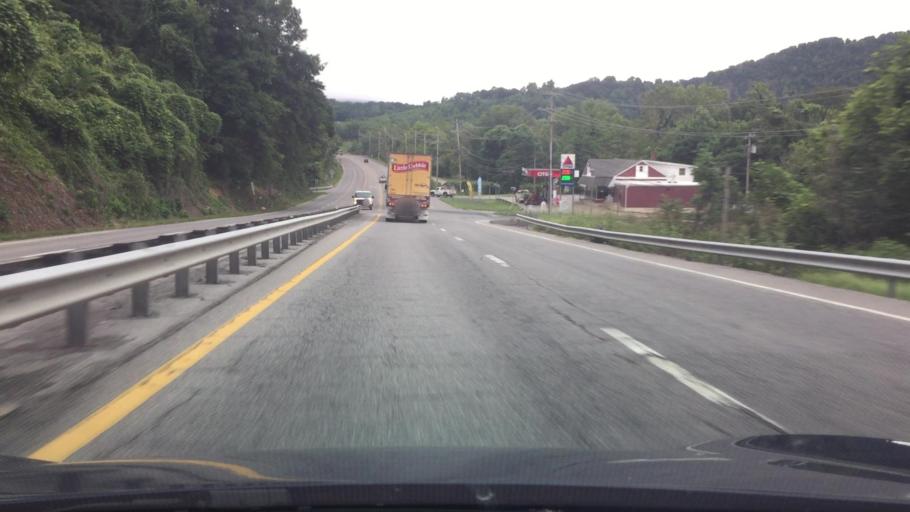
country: US
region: Virginia
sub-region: Montgomery County
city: Shawsville
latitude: 37.2454
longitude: -80.1766
